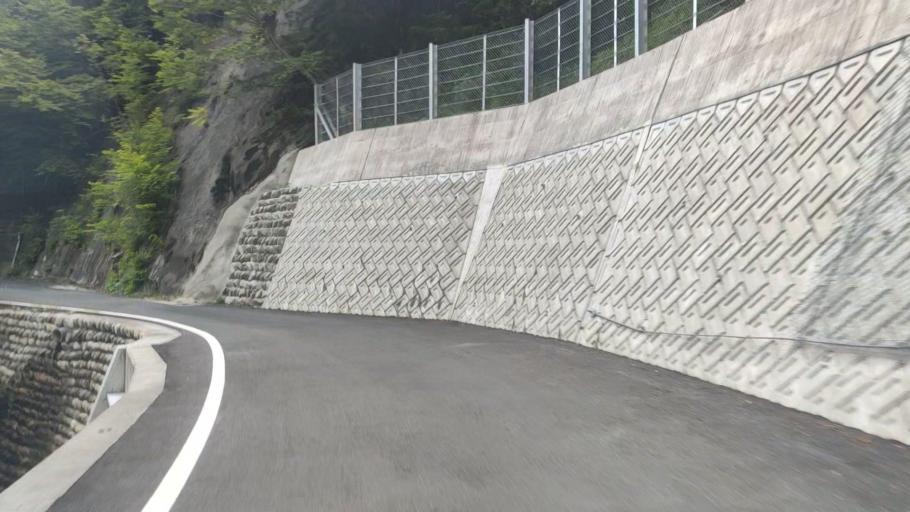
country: JP
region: Gifu
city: Godo
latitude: 35.6940
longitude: 136.5892
